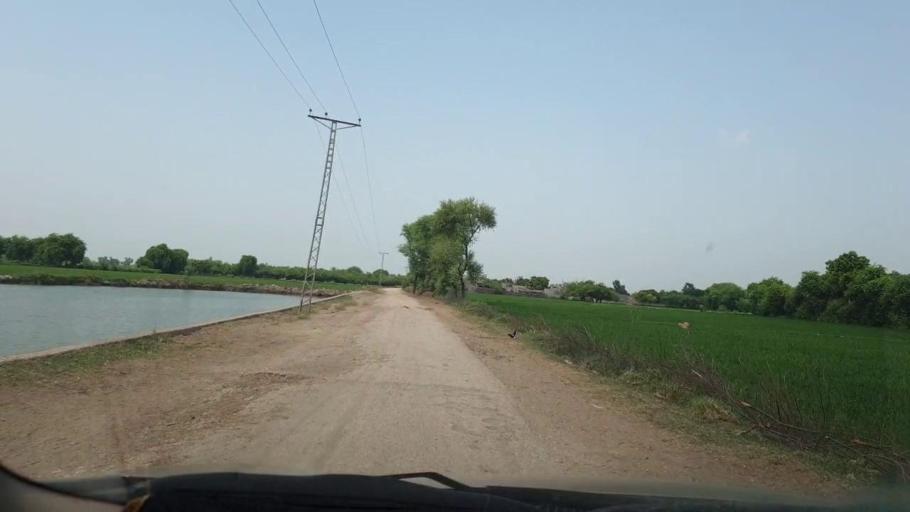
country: PK
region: Sindh
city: Larkana
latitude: 27.5841
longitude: 68.1443
